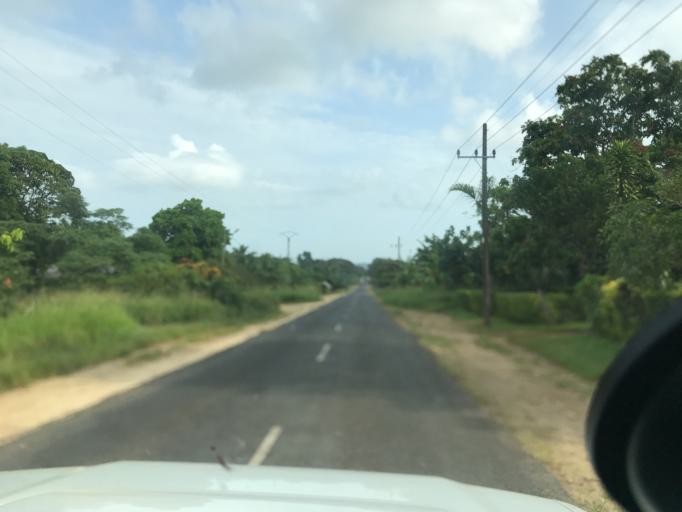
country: VU
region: Sanma
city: Luganville
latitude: -15.4981
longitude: 167.1922
